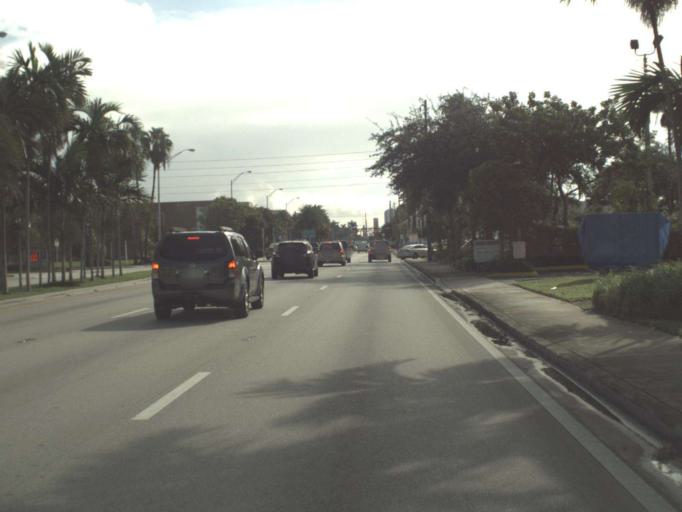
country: US
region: Florida
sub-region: Miami-Dade County
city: North Miami Beach
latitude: 25.9259
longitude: -80.1589
